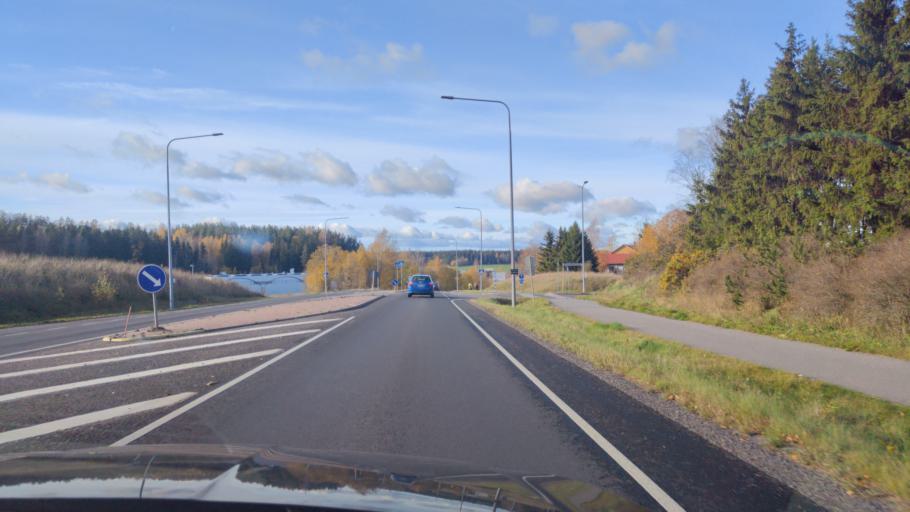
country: FI
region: Varsinais-Suomi
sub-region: Turku
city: Kaarina
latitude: 60.4624
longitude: 22.3550
